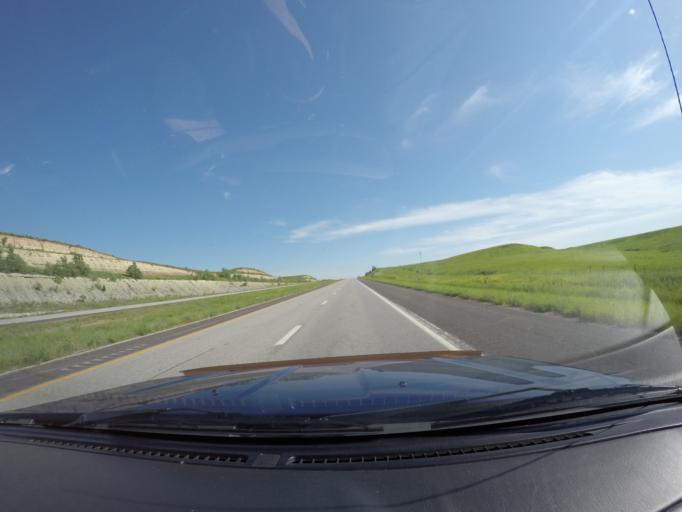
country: US
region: Kansas
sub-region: Riley County
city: Manhattan
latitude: 39.0766
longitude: -96.5385
